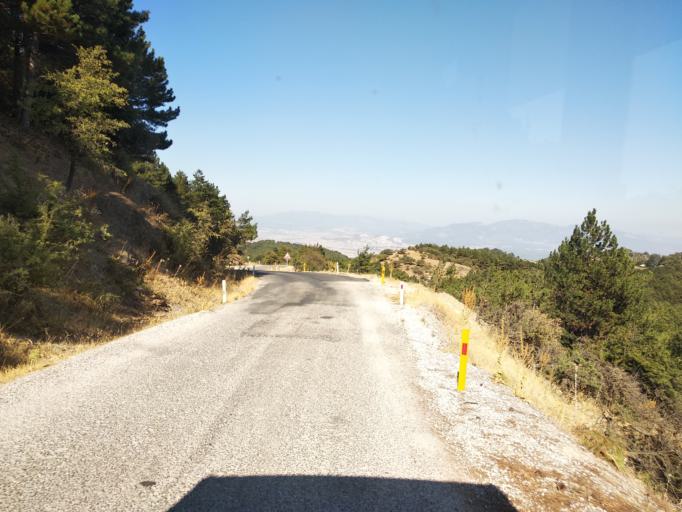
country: TR
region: Izmir
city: Gaziemir
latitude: 38.3174
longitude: 27.0102
